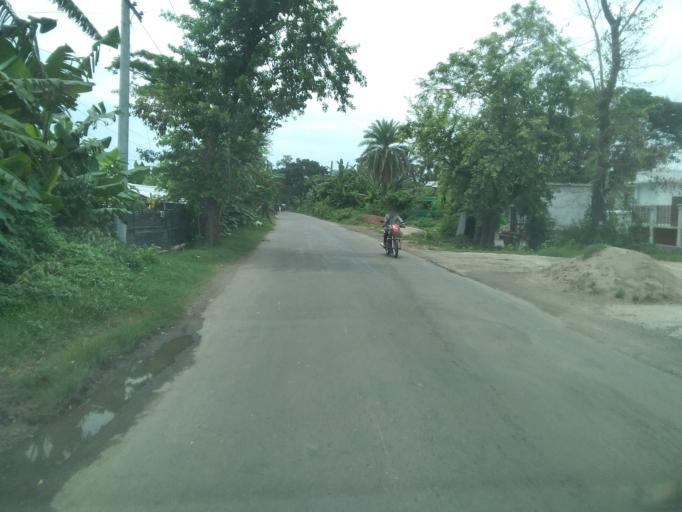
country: IN
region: West Bengal
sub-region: North 24 Parganas
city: Taki
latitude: 22.5789
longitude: 88.9983
